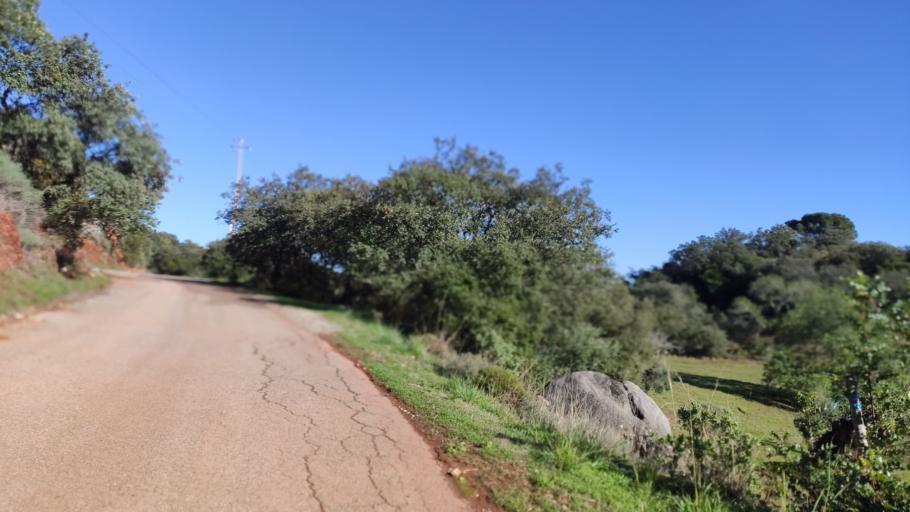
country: PT
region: Faro
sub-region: Sao Bras de Alportel
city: Sao Bras de Alportel
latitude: 37.1581
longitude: -7.9038
